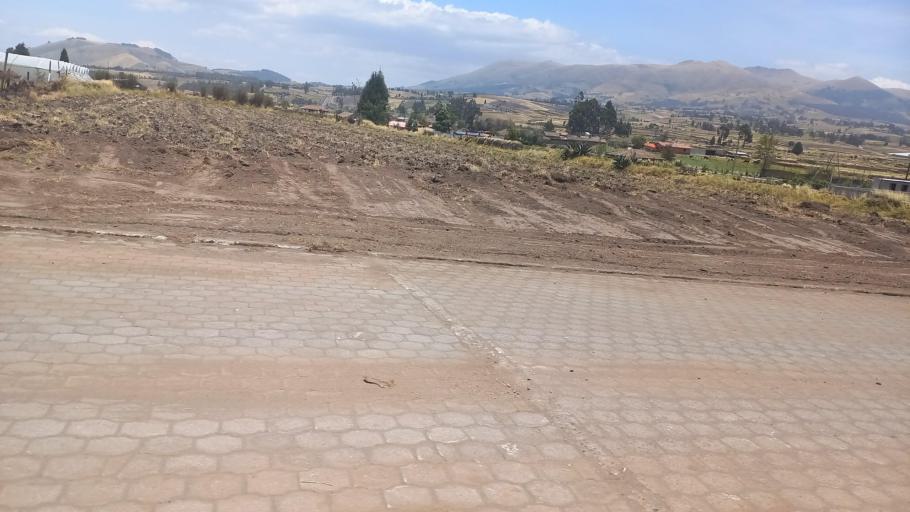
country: EC
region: Pichincha
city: Cayambe
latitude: 0.1428
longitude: -78.0694
